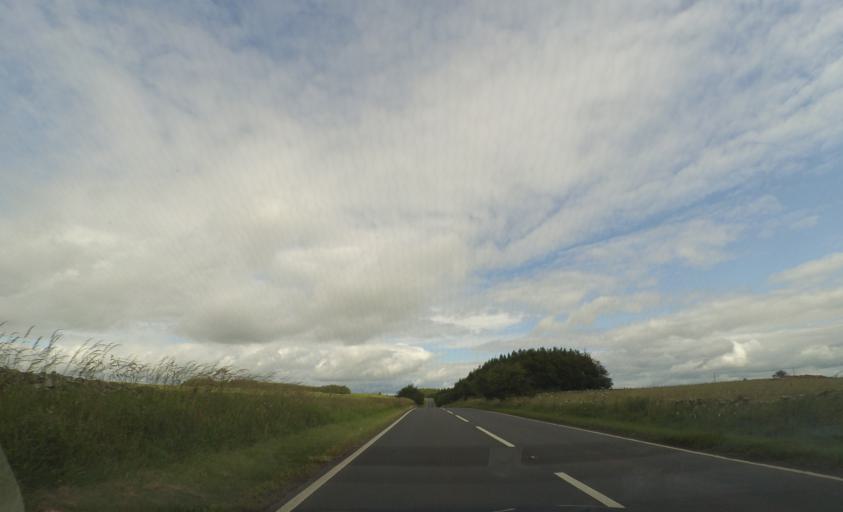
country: GB
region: Scotland
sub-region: The Scottish Borders
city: Hawick
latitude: 55.4660
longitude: -2.7890
